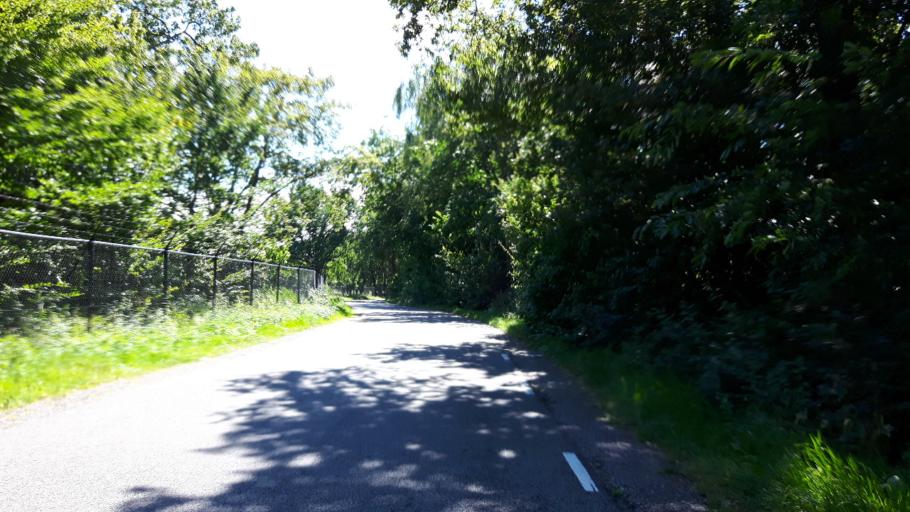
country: NL
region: North Holland
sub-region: Gemeente Wijdemeren
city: Nieuw-Loosdrecht
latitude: 52.1934
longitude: 5.1537
